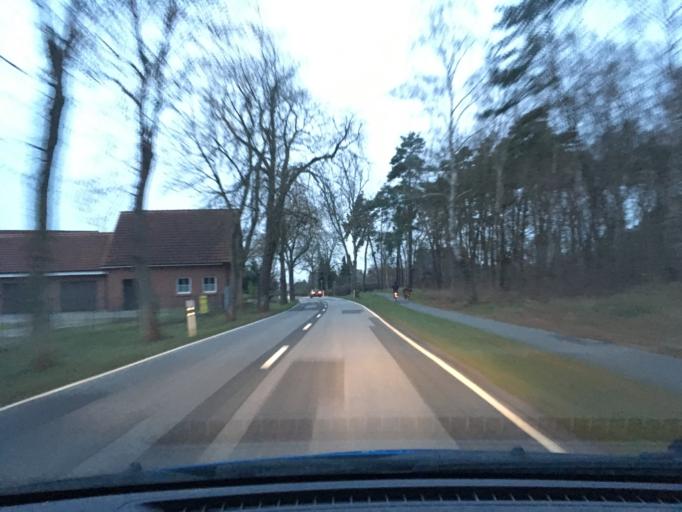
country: DE
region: Mecklenburg-Vorpommern
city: Boizenburg
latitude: 53.3651
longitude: 10.7678
